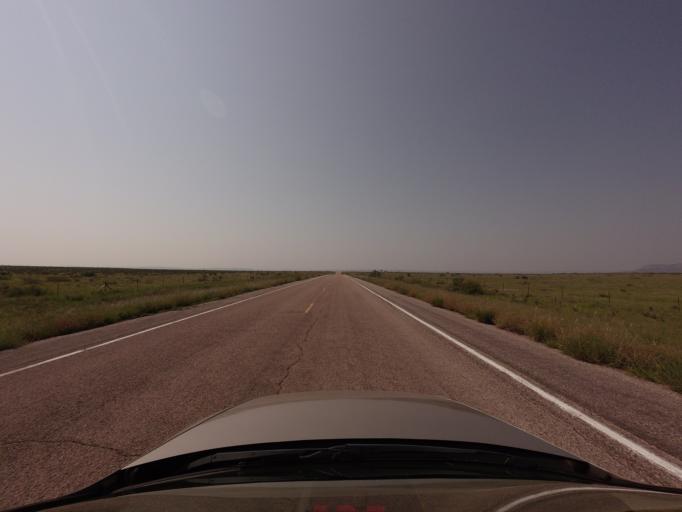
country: US
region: New Mexico
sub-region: Quay County
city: Tucumcari
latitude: 34.9635
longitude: -103.7555
